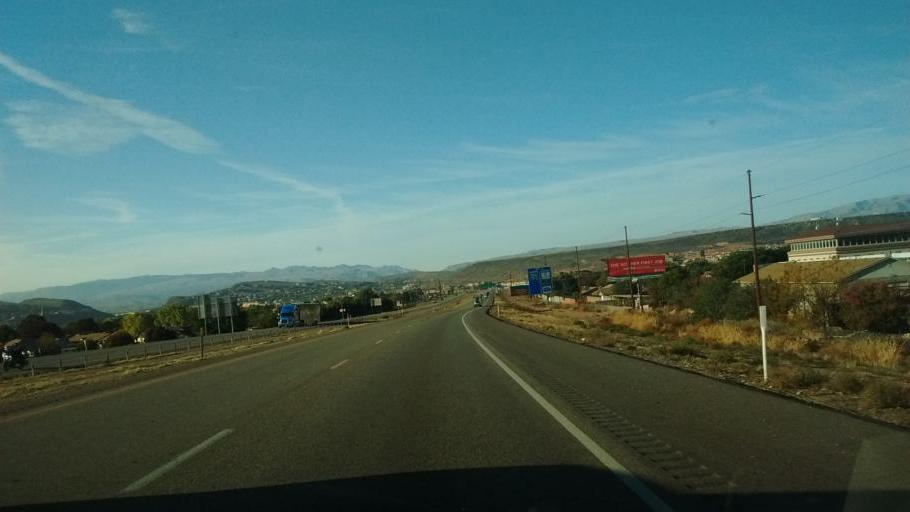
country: US
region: Utah
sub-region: Washington County
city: Saint George
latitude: 37.0957
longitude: -113.5667
